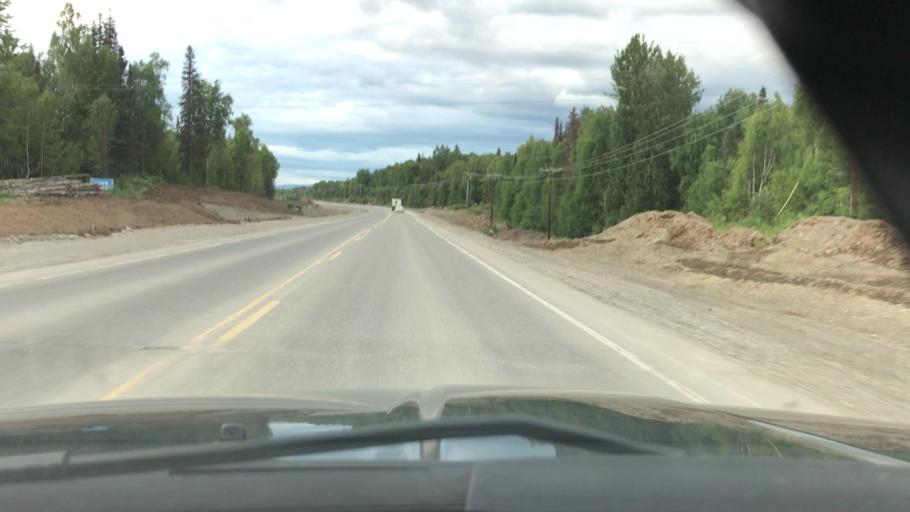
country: US
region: Alaska
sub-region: Matanuska-Susitna Borough
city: Y
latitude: 62.1116
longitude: -150.0547
